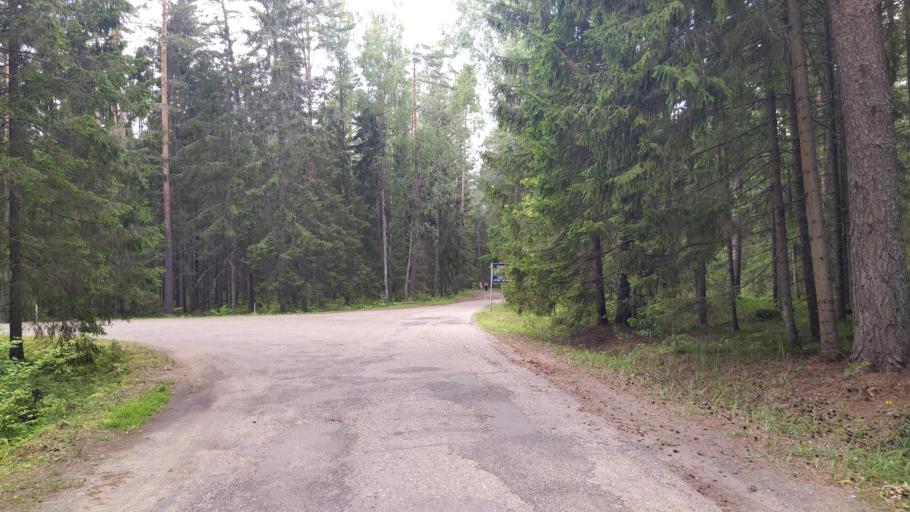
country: RU
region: Pskov
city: Pushkinskiye Gory
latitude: 57.0582
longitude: 28.9404
